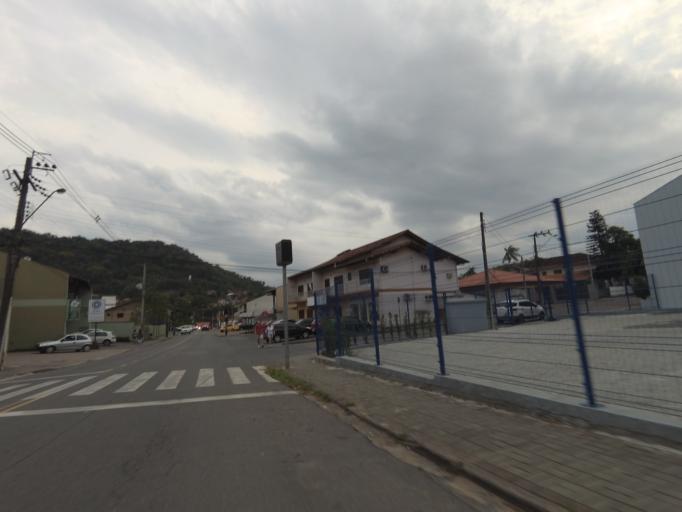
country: BR
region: Santa Catarina
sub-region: Blumenau
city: Blumenau
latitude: -26.8711
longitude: -49.0497
